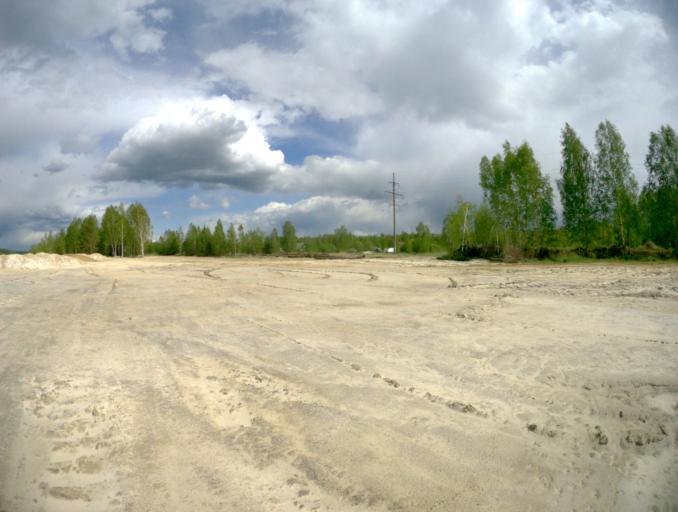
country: RU
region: Vladimir
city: Velikodvorskiy
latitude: 55.2274
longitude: 40.6399
